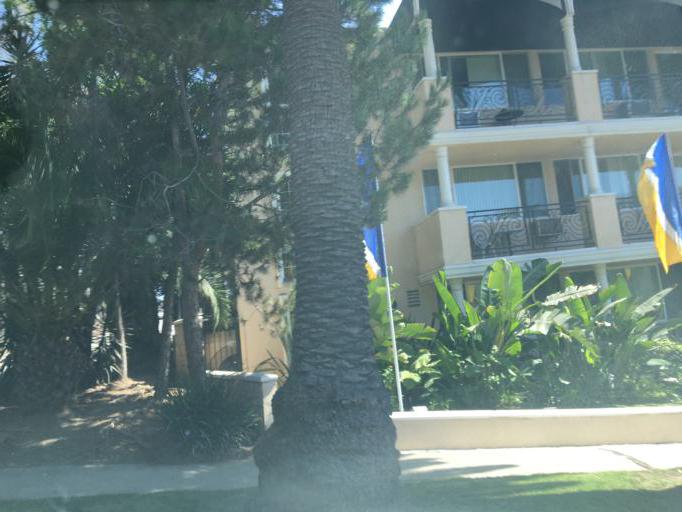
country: US
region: California
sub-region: Los Angeles County
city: Westwood, Los Angeles
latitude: 34.0569
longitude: -118.4647
